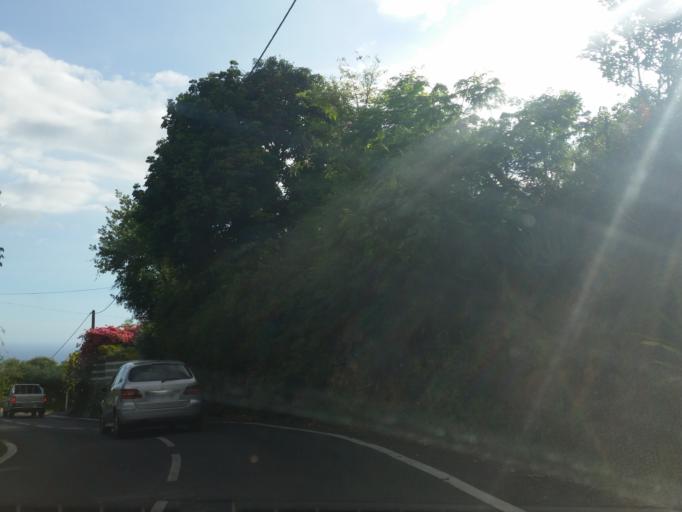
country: RE
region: Reunion
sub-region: Reunion
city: L'Entre-Deux
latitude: -21.2497
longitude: 55.4760
